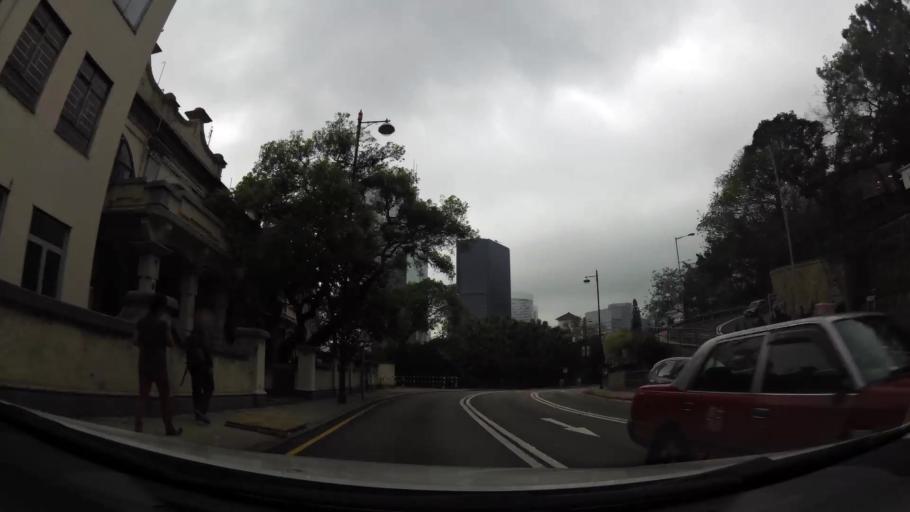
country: HK
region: Central and Western
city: Central
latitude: 22.2793
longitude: 114.1558
